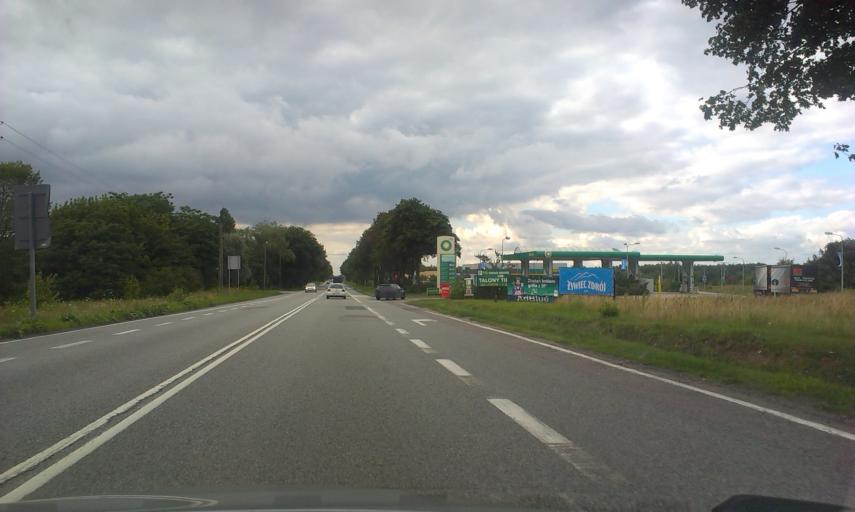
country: PL
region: Masovian Voivodeship
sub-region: Powiat zyrardowski
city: Mszczonow
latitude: 51.9983
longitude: 20.4954
